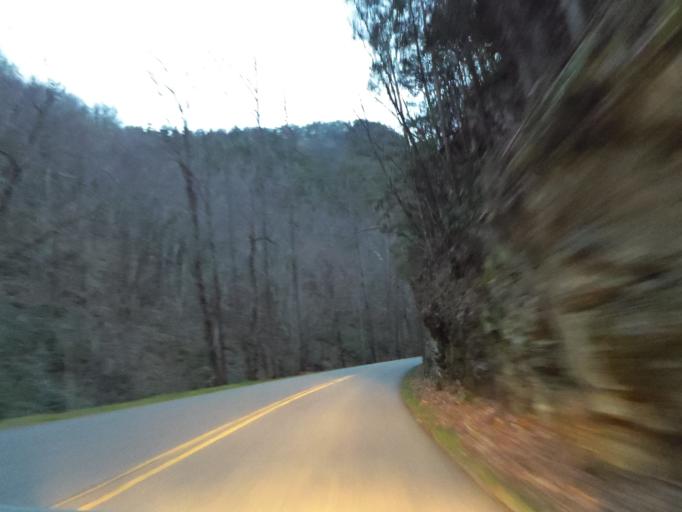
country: US
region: Tennessee
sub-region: Sevier County
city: Pigeon Forge
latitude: 35.6463
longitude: -83.7187
